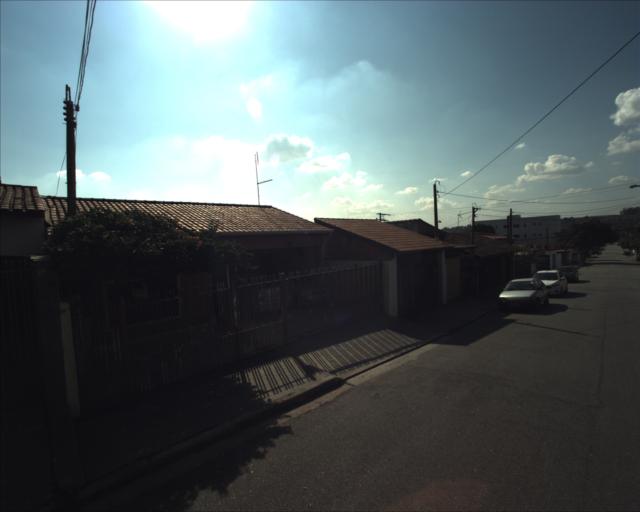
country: BR
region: Sao Paulo
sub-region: Sorocaba
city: Sorocaba
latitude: -23.4765
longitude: -47.4489
